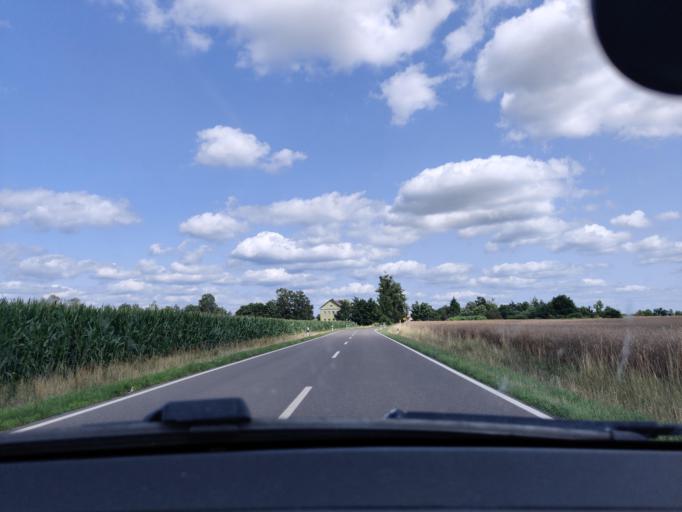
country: DE
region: Saxony-Anhalt
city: Loburg
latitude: 52.0779
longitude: 12.0330
